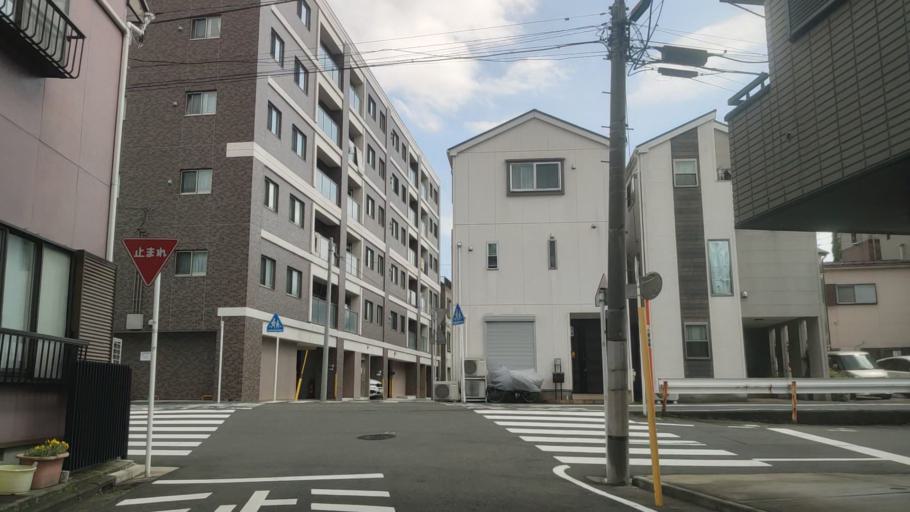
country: JP
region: Kanagawa
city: Yokohama
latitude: 35.4332
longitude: 139.6550
